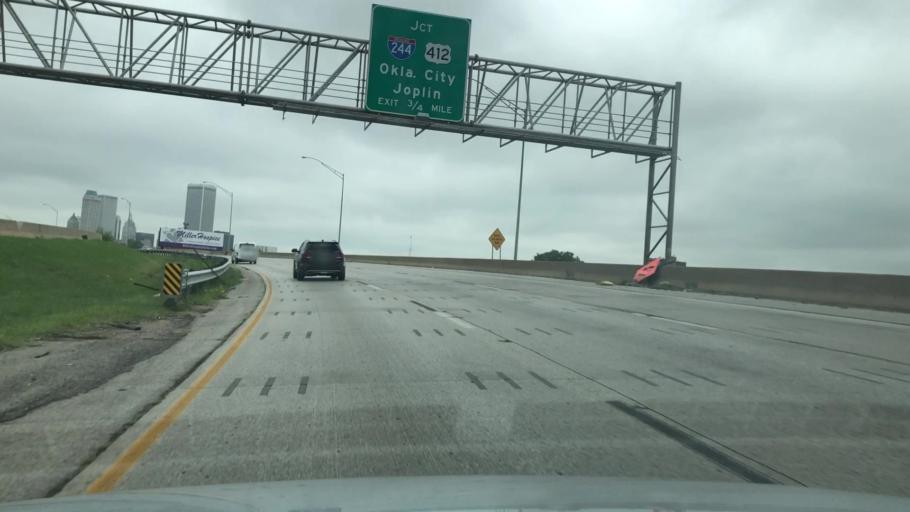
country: US
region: Oklahoma
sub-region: Tulsa County
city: Tulsa
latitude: 36.1727
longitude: -95.9795
